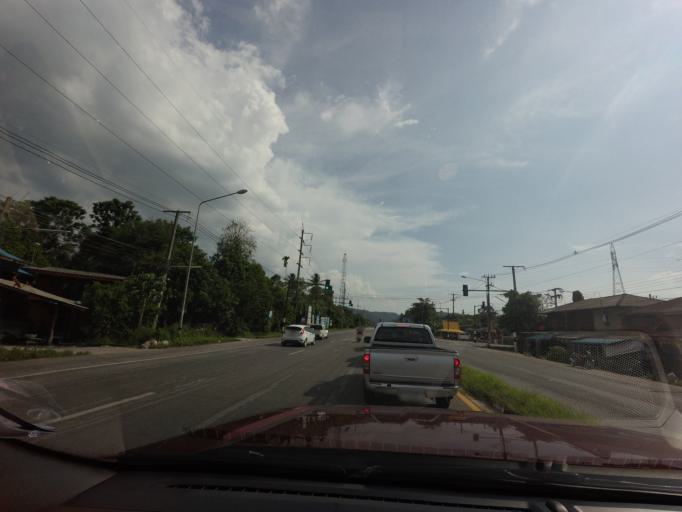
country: TH
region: Yala
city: Yala
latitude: 6.5473
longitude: 101.2530
